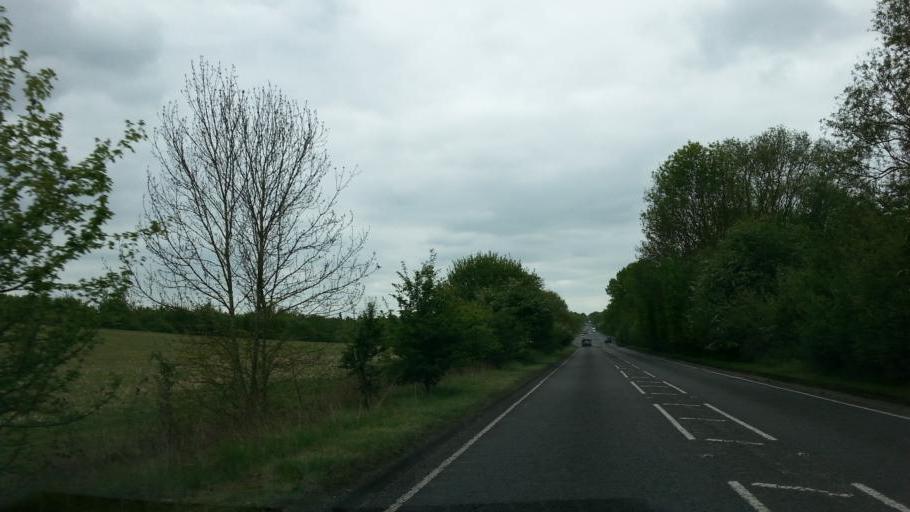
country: GB
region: England
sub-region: Suffolk
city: Hadleigh
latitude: 52.0555
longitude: 0.9566
